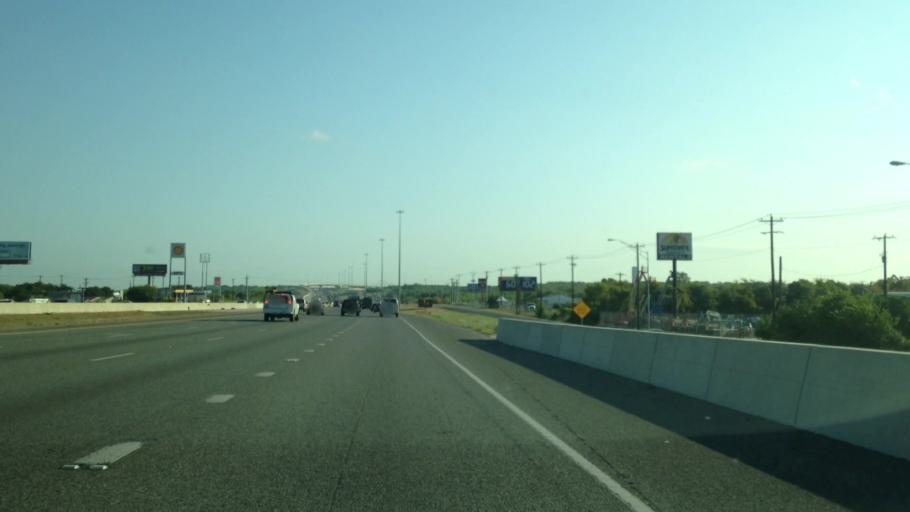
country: US
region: Texas
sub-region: Hays County
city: Buda
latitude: 30.0907
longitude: -97.8171
